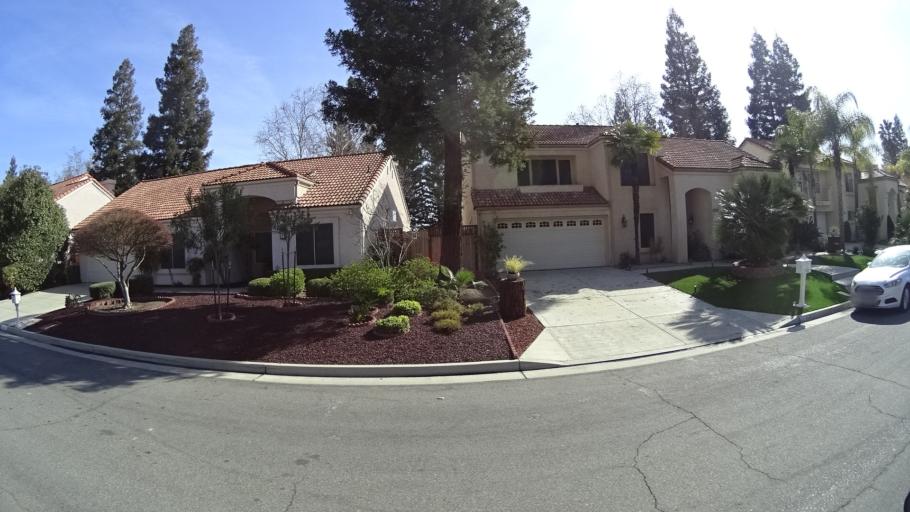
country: US
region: California
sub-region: Fresno County
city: Clovis
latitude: 36.8875
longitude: -119.7760
